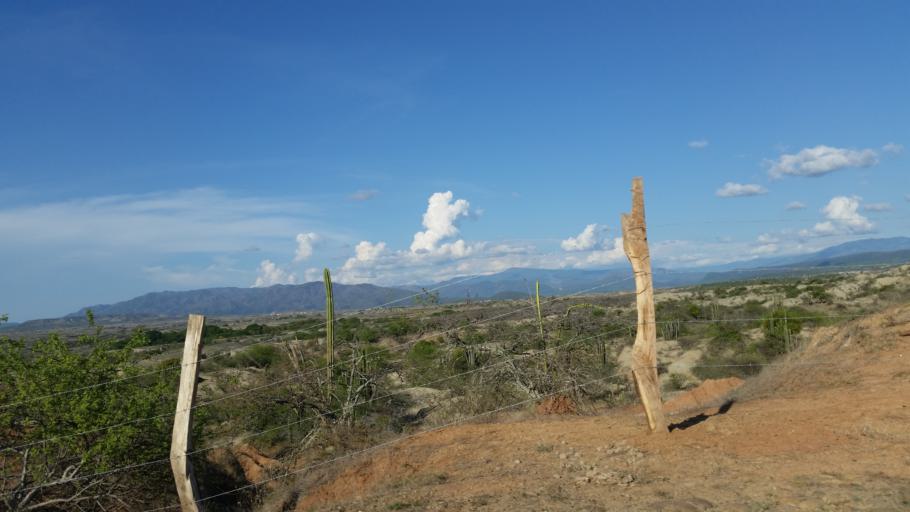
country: CO
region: Huila
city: Villavieja
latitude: 3.2298
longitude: -75.1518
